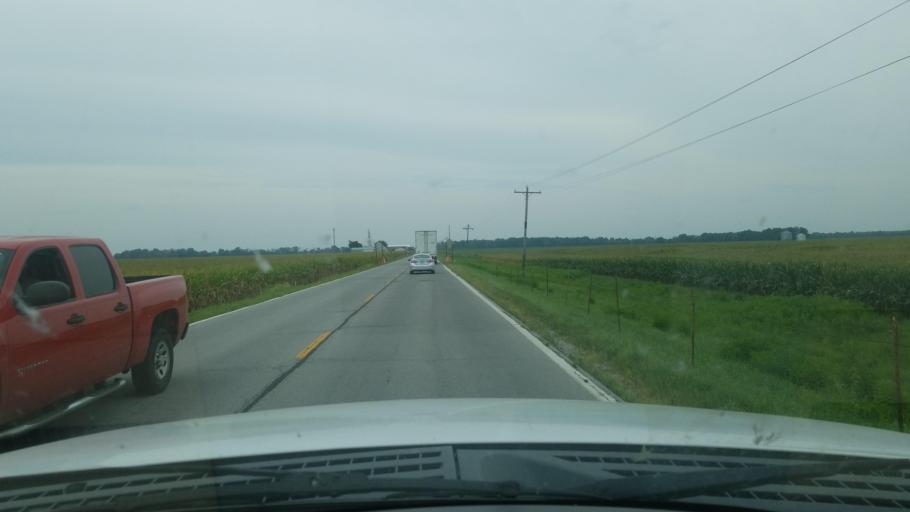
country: US
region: Illinois
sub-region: Saline County
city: Eldorado
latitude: 37.8649
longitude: -88.4528
